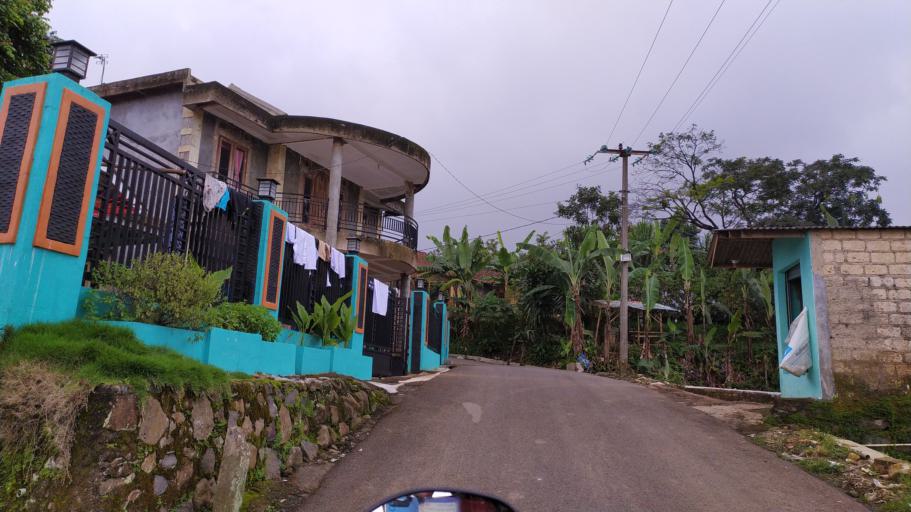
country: ID
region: West Java
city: Ciampea
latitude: -6.6357
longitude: 106.7068
